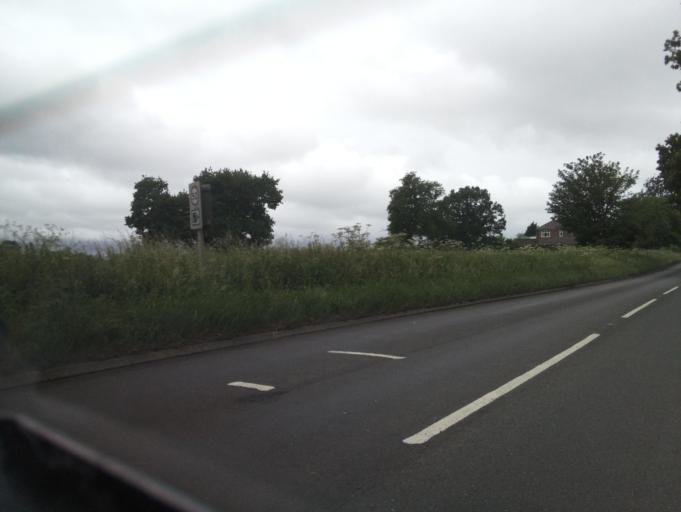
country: GB
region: England
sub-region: Staffordshire
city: Burton upon Trent
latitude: 52.8408
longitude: -1.6687
